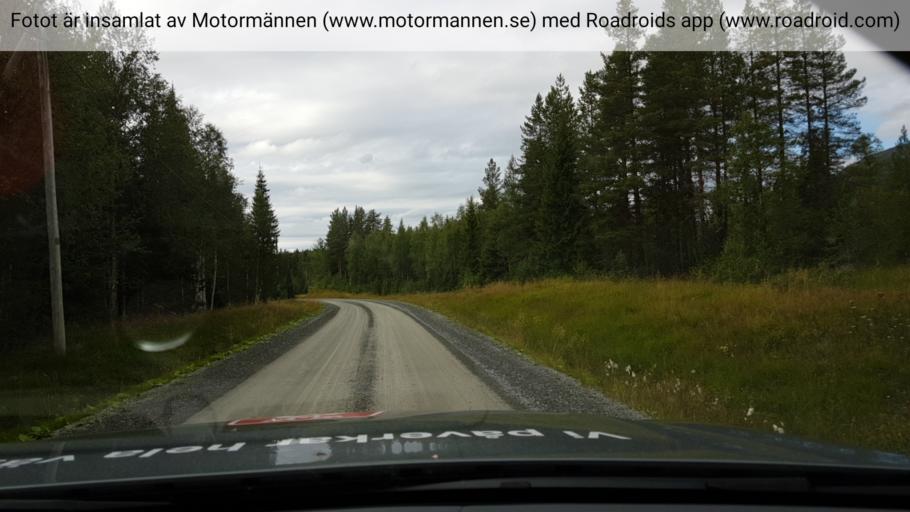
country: SE
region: Jaemtland
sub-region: Krokoms Kommun
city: Valla
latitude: 63.7107
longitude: 13.5442
